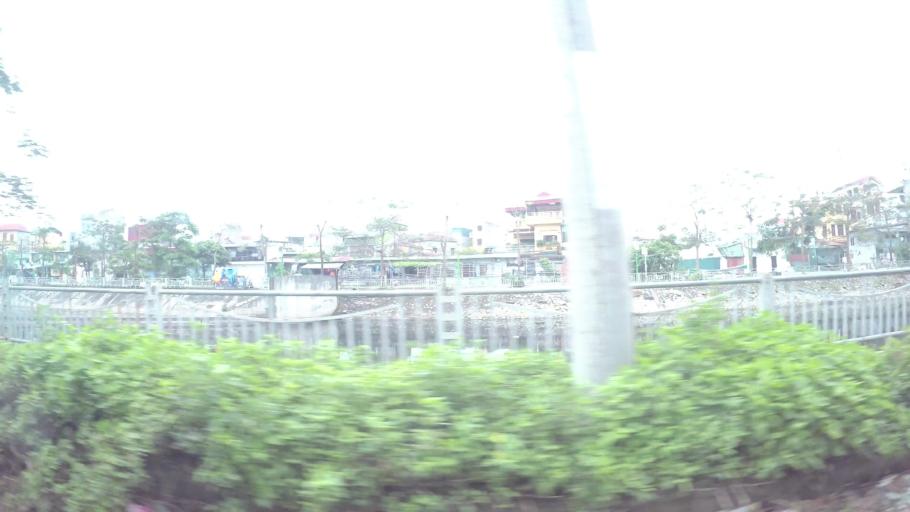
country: VN
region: Ha Noi
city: Van Dien
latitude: 20.9725
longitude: 105.8528
